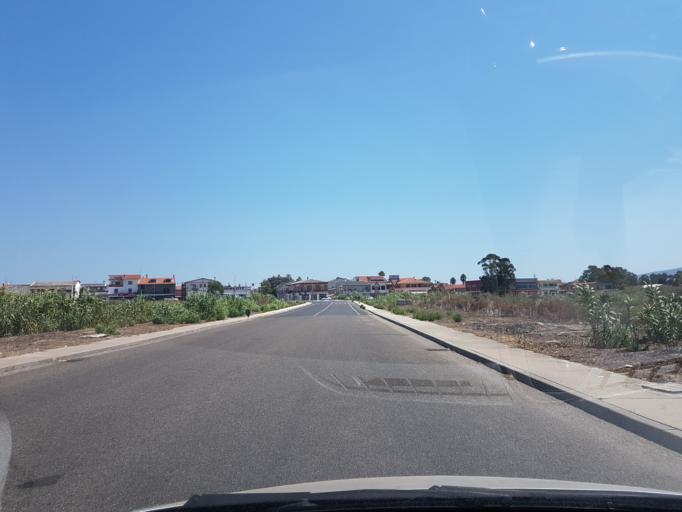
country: IT
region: Sardinia
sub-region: Provincia di Oristano
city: Santa Giusta
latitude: 39.8864
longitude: 8.6004
